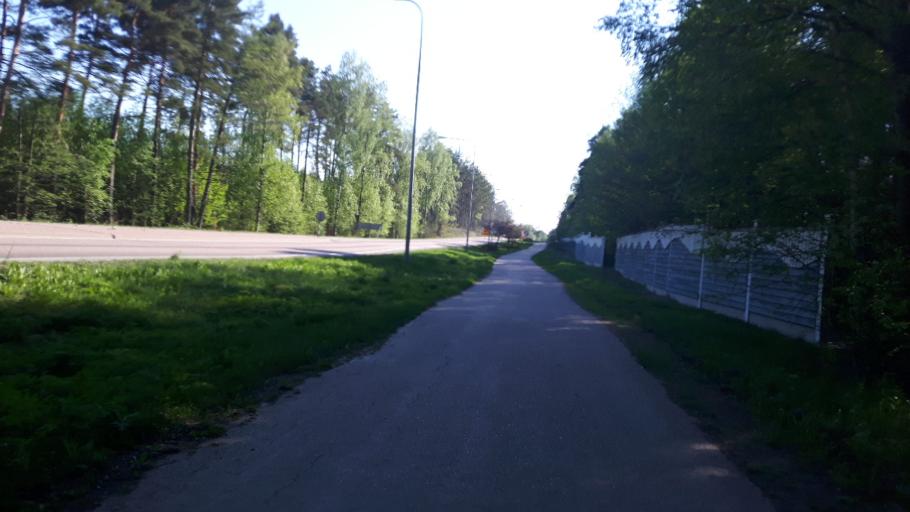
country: FI
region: Kymenlaakso
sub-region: Kotka-Hamina
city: Kotka
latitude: 60.4434
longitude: 26.8882
